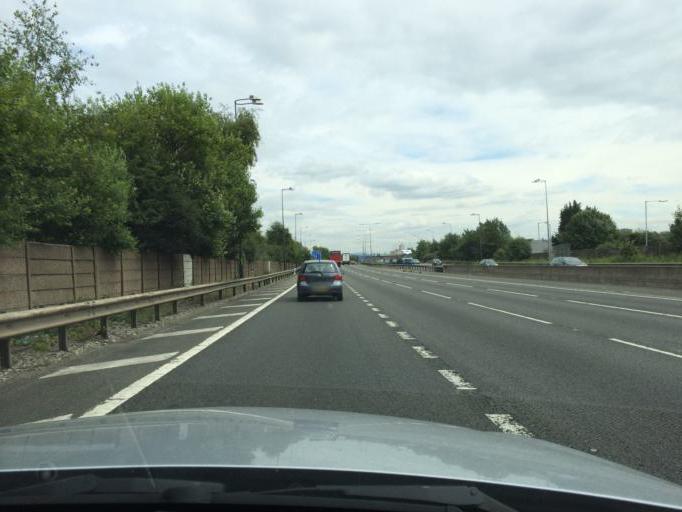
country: GB
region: England
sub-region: Borough of Stockport
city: Cheadle Heath
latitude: 53.4078
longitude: -2.1847
